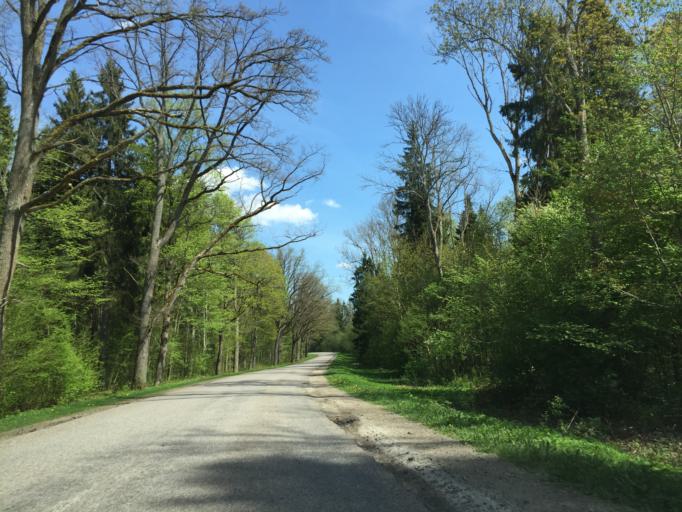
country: LV
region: Krimulda
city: Ragana
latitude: 57.3365
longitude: 24.6497
